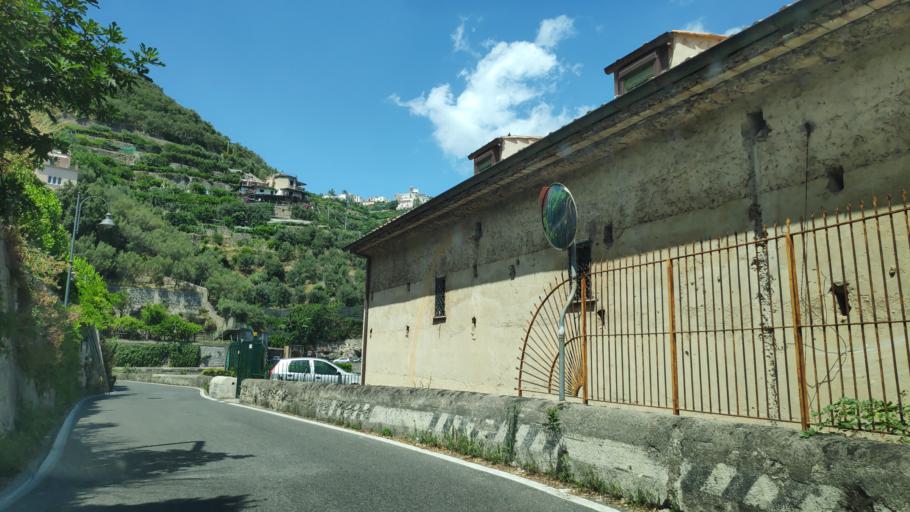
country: IT
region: Campania
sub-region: Provincia di Salerno
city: Ravello
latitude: 40.6427
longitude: 14.6182
